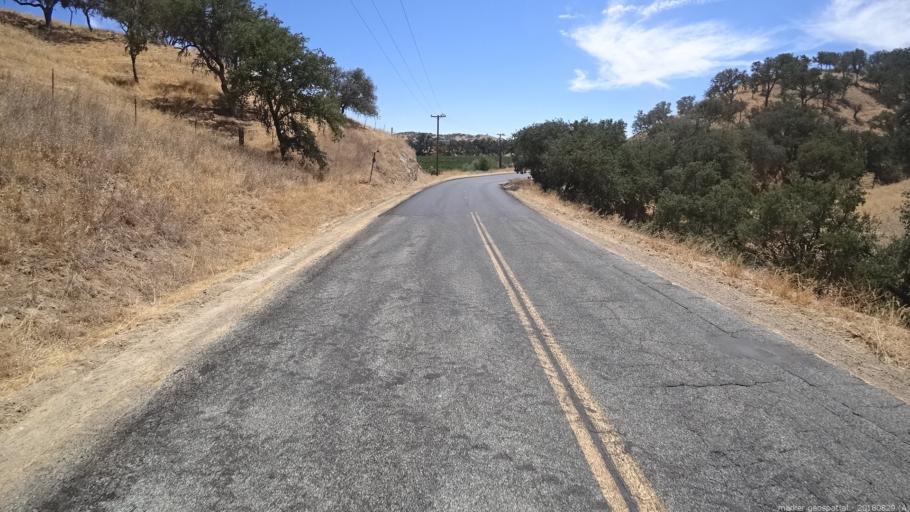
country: US
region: California
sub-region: San Luis Obispo County
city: Lake Nacimiento
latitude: 35.8205
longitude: -120.8414
